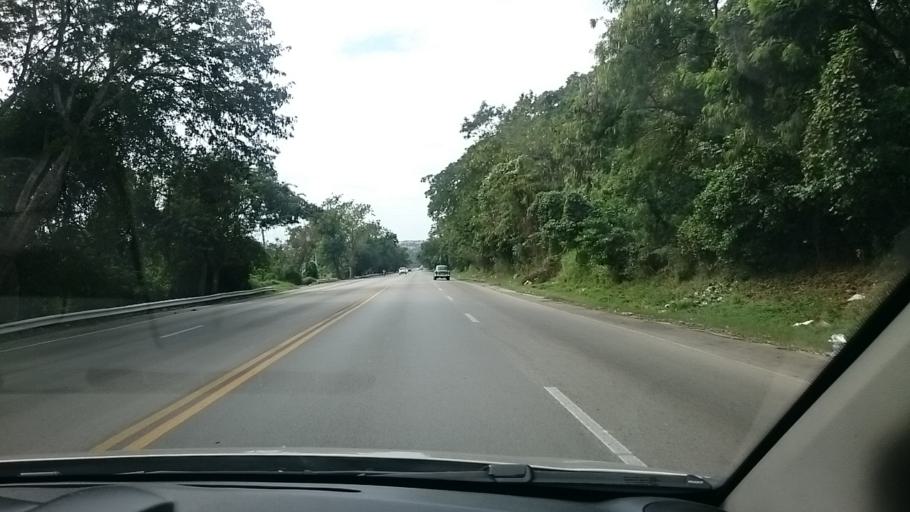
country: CU
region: La Habana
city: Alamar
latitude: 23.1511
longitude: -82.2761
